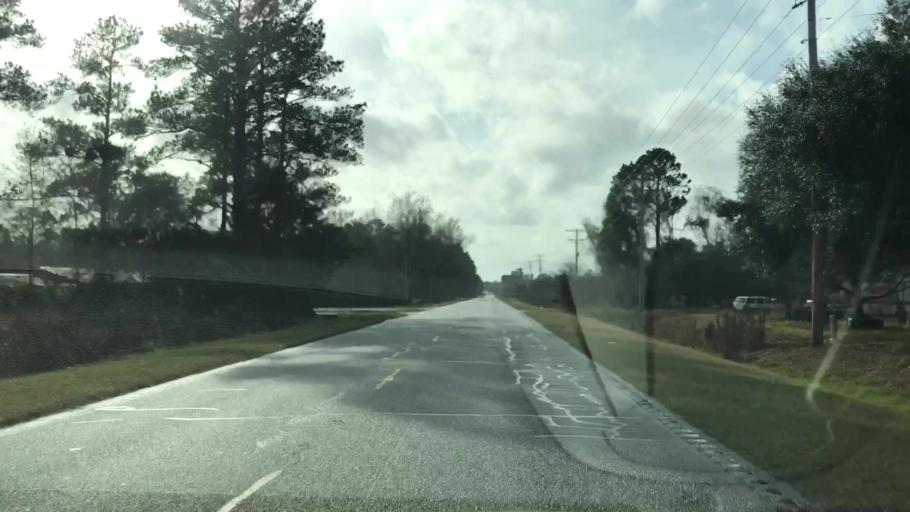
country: US
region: South Carolina
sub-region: Williamsburg County
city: Andrews
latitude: 33.5012
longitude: -79.5291
